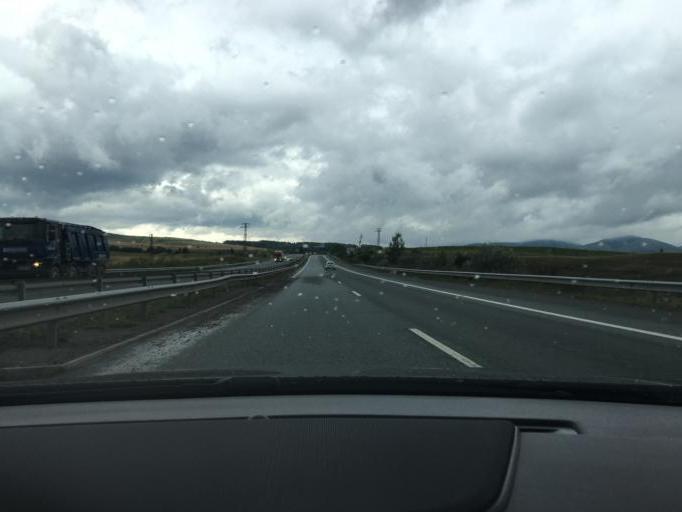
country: BG
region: Pernik
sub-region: Obshtina Pernik
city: Pernik
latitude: 42.5863
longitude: 23.1203
